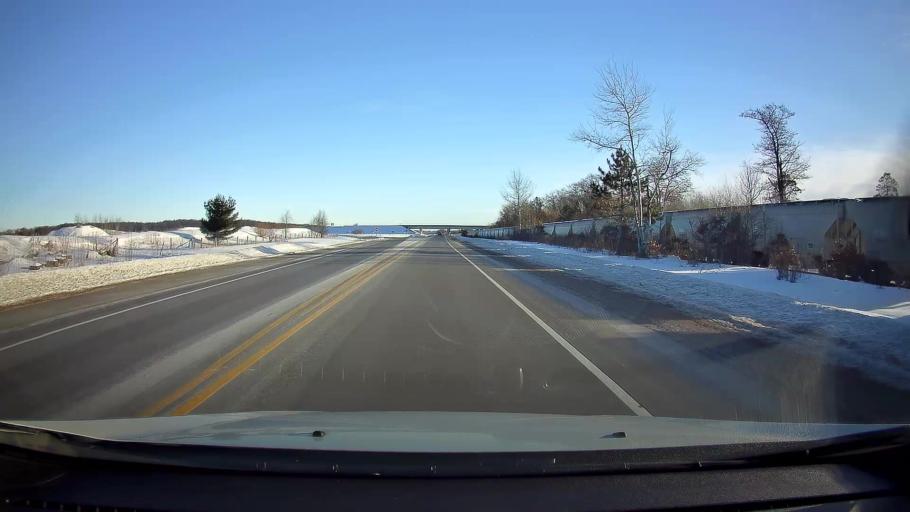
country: US
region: Wisconsin
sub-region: Washburn County
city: Spooner
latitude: 45.8496
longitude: -91.8638
